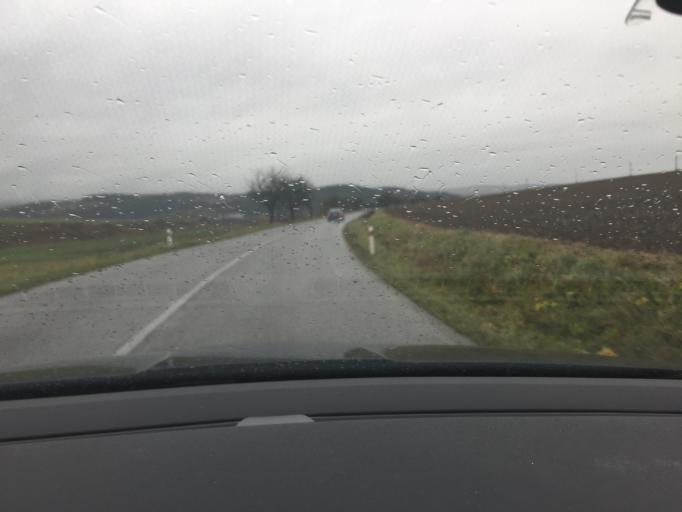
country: SK
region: Presovsky
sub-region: Okres Presov
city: Kezmarok
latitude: 49.1638
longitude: 20.4186
